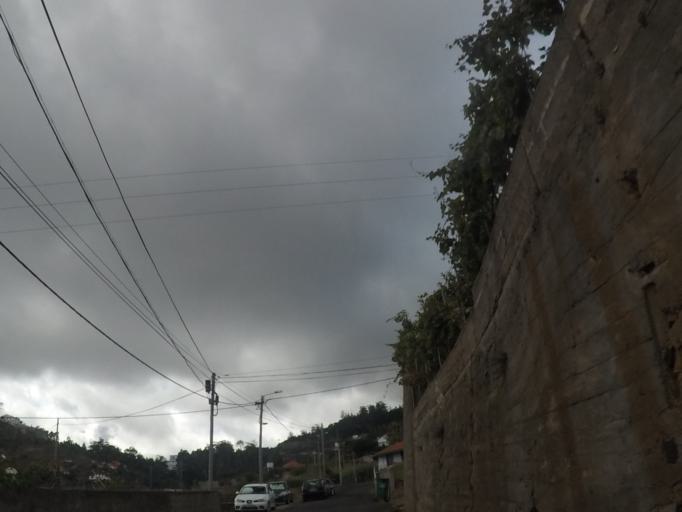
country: PT
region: Madeira
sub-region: Santa Cruz
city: Camacha
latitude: 32.6632
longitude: -16.8283
